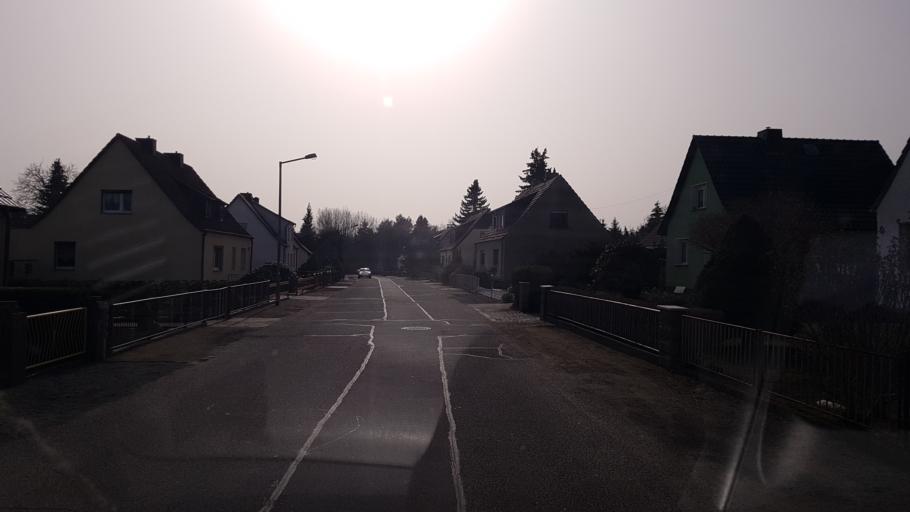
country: DE
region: Brandenburg
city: Lauchhammer
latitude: 51.5042
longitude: 13.7872
